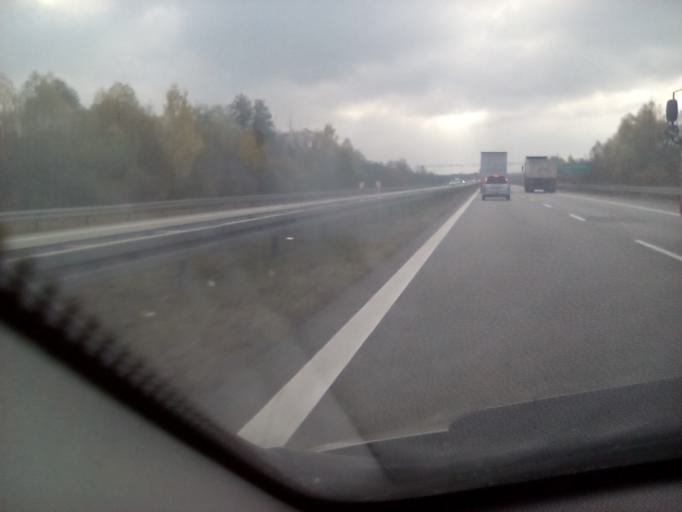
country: PL
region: Masovian Voivodeship
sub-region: Powiat bialobrzeski
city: Promna
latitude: 51.6678
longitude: 20.9532
